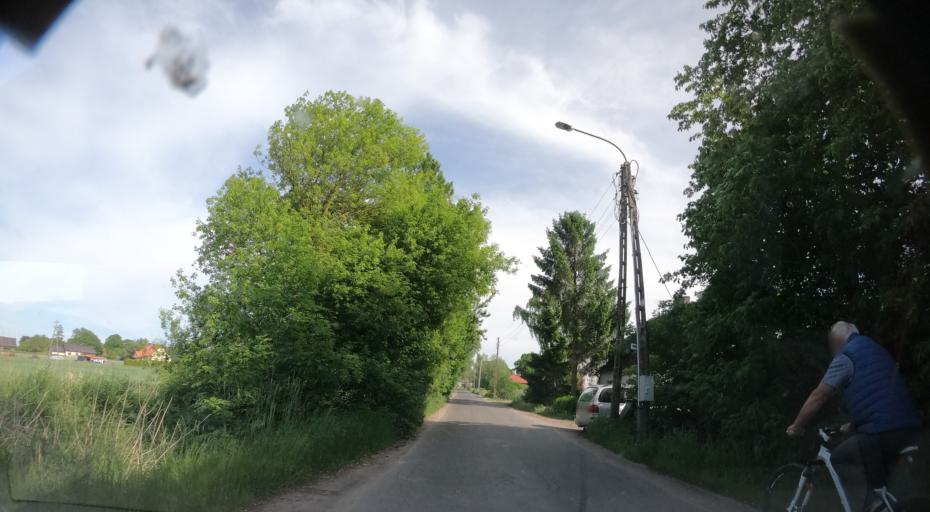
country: PL
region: West Pomeranian Voivodeship
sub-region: Koszalin
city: Koszalin
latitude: 54.2475
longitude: 16.1625
